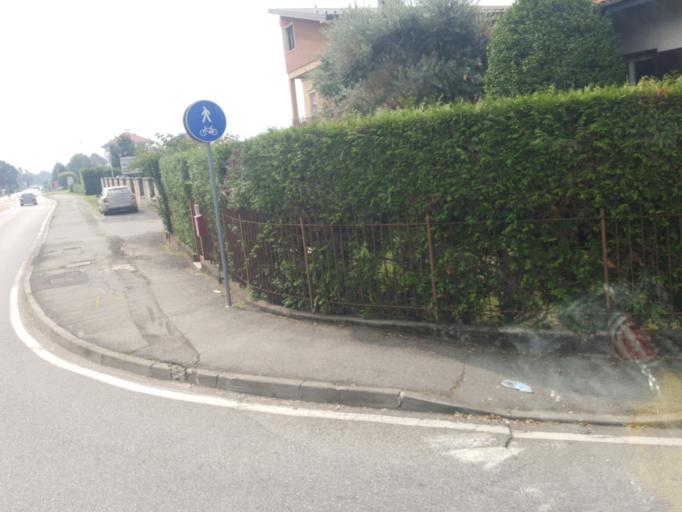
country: IT
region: Lombardy
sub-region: Provincia di Varese
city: Gorla Maggiore
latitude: 45.6635
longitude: 8.8969
